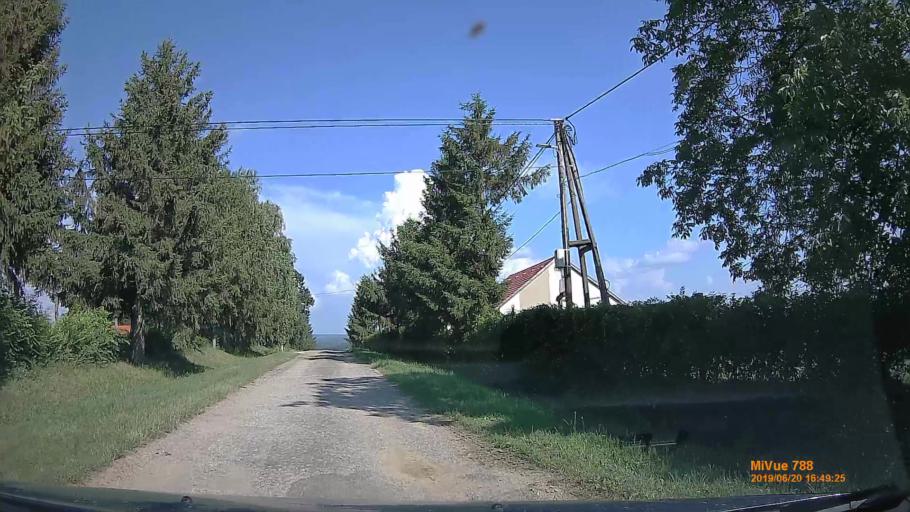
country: HU
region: Baranya
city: Buekkoesd
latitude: 46.1599
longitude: 18.0389
